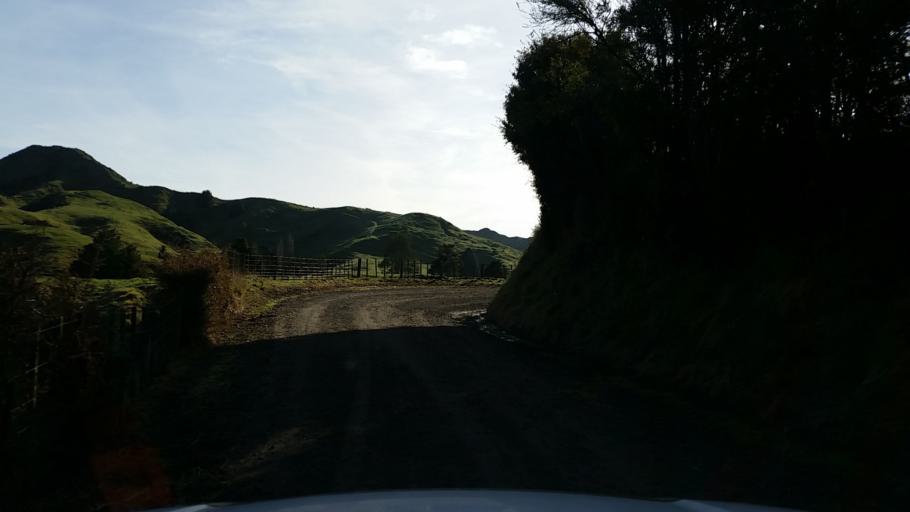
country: NZ
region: Taranaki
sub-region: South Taranaki District
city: Eltham
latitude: -39.3151
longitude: 174.5342
